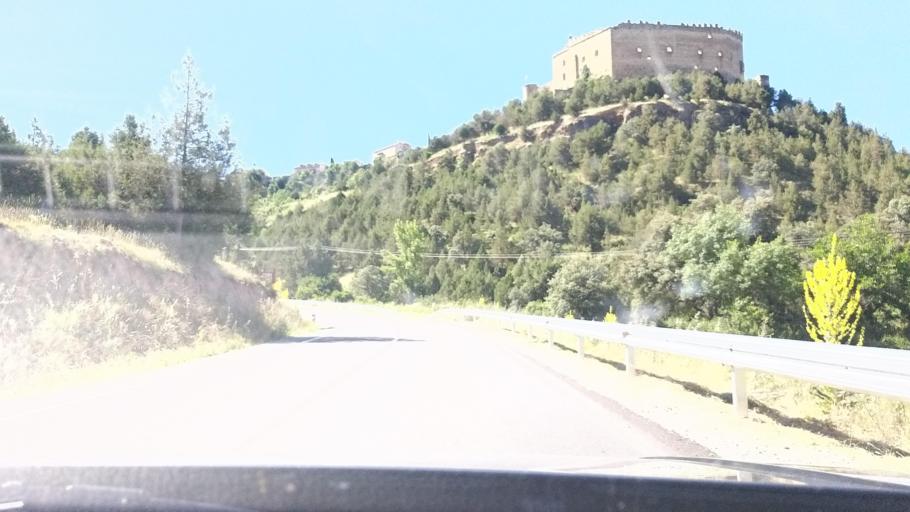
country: ES
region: Castille and Leon
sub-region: Provincia de Segovia
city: Pedraza
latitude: 41.1350
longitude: -3.8147
